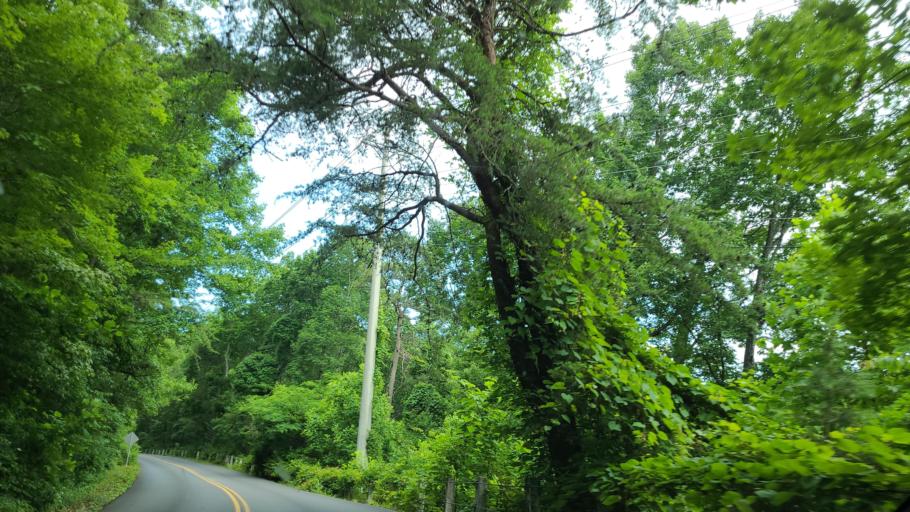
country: US
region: Tennessee
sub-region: Hamilton County
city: Lookout Mountain
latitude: 34.9874
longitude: -85.3445
